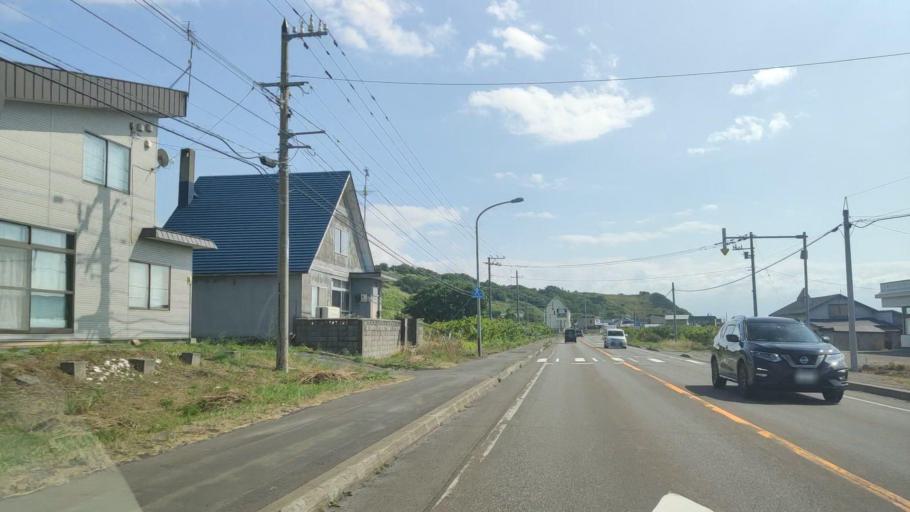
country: JP
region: Hokkaido
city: Rumoi
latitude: 43.9678
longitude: 141.6464
